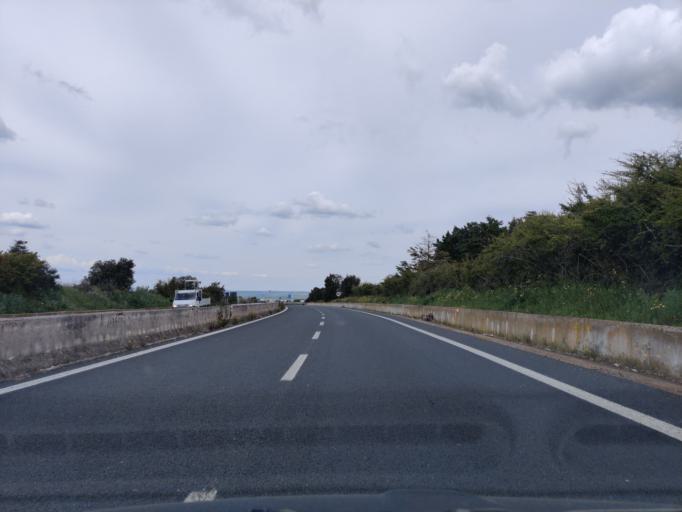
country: IT
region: Latium
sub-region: Citta metropolitana di Roma Capitale
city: Aurelia
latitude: 42.1356
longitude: 11.7950
